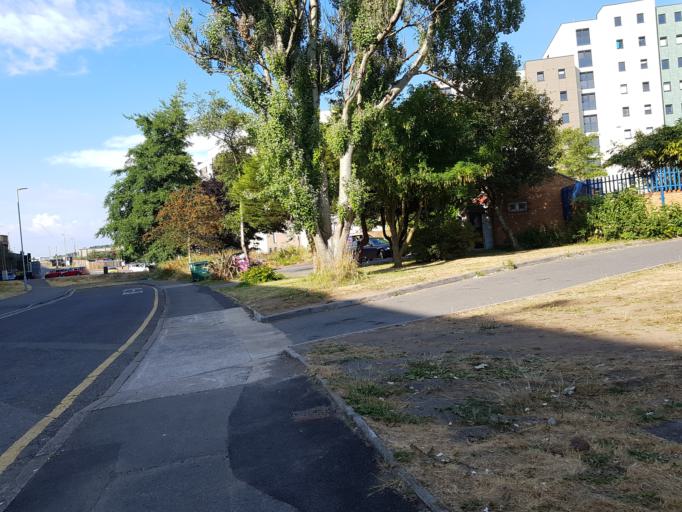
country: GB
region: Wales
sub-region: City and County of Swansea
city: Swansea
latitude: 51.6259
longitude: -3.9394
